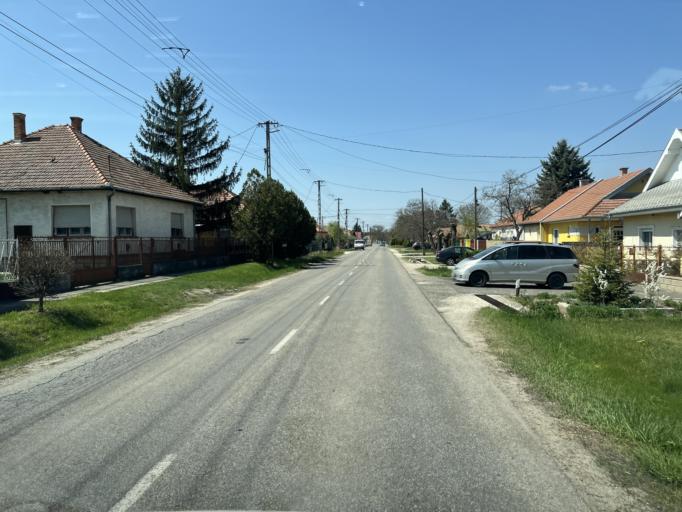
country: HU
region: Pest
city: Kakucs
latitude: 47.2447
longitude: 19.3505
